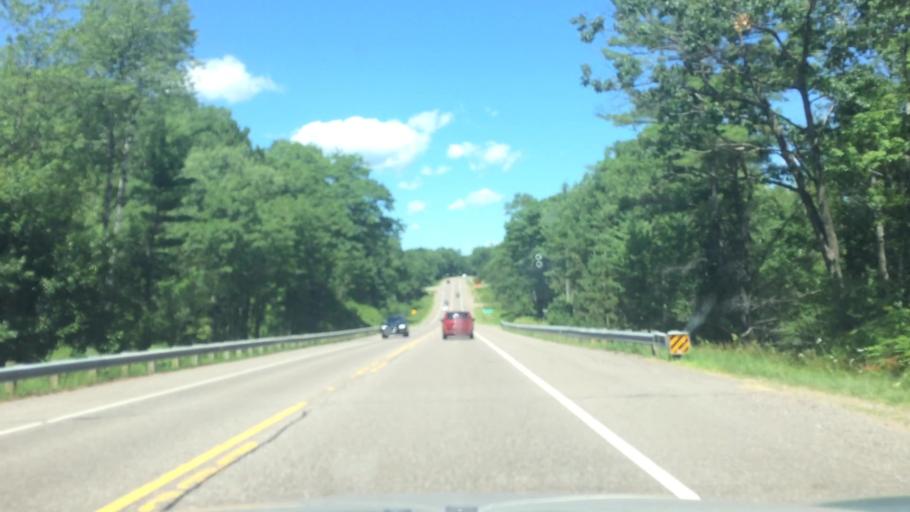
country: US
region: Wisconsin
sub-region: Vilas County
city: Lac du Flambeau
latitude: 45.7747
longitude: -89.7157
